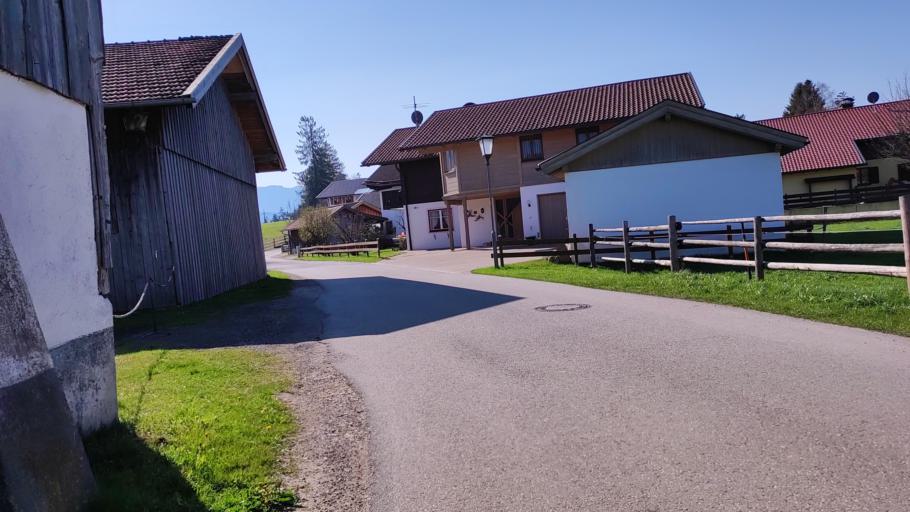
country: DE
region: Bavaria
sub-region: Upper Bavaria
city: Saulgrub
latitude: 47.6480
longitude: 11.0150
